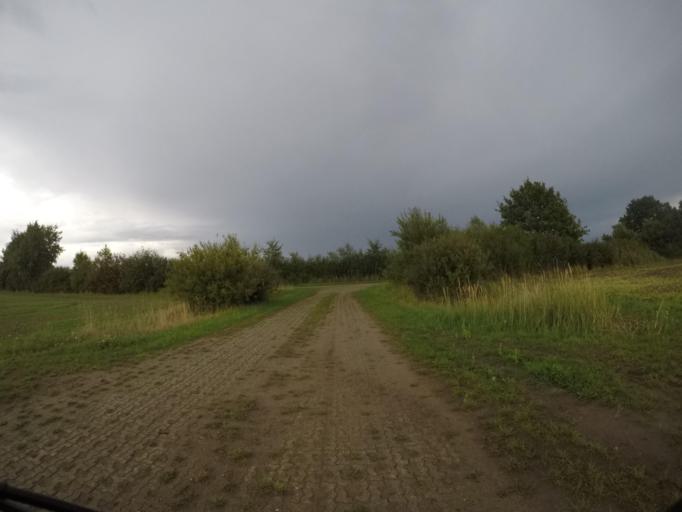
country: DE
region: Lower Saxony
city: Neu Darchau
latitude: 53.2639
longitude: 10.9046
